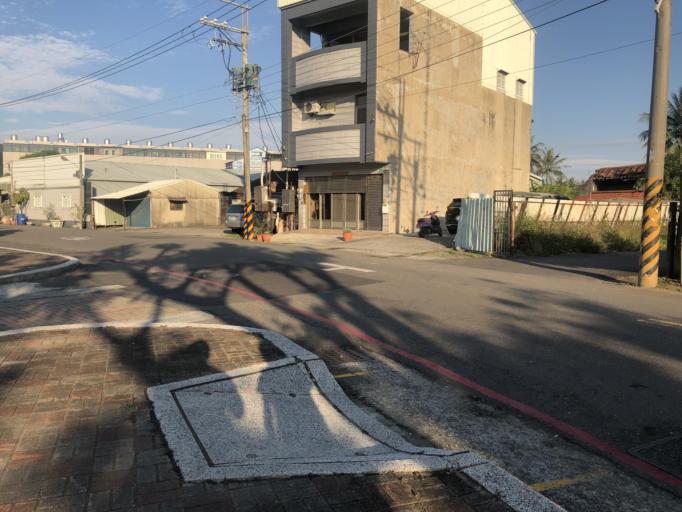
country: TW
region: Taiwan
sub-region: Tainan
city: Tainan
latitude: 23.0374
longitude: 120.1837
